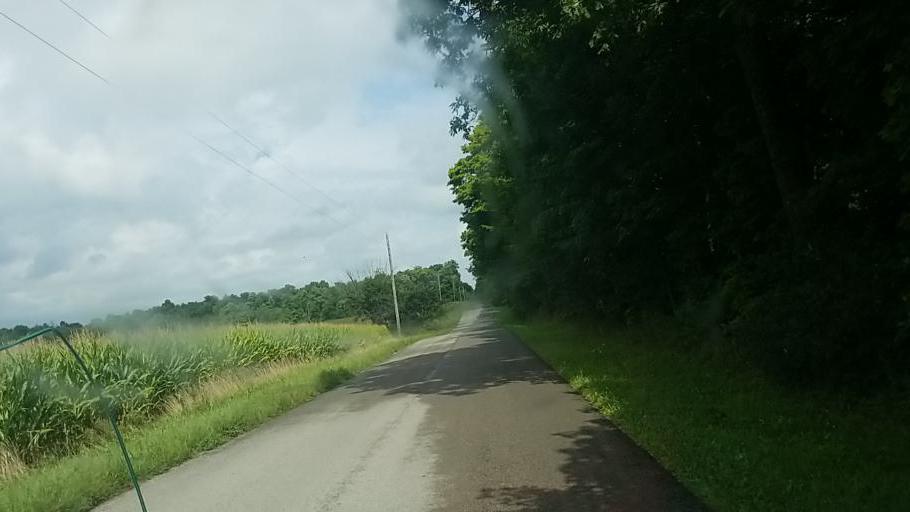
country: US
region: Ohio
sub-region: Champaign County
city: North Lewisburg
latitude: 40.2641
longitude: -83.6165
